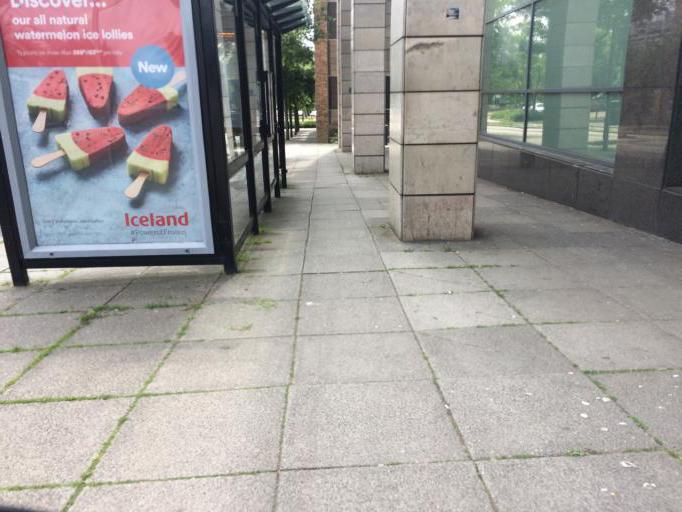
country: GB
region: England
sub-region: Milton Keynes
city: Milton Keynes
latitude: 52.0409
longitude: -0.7559
